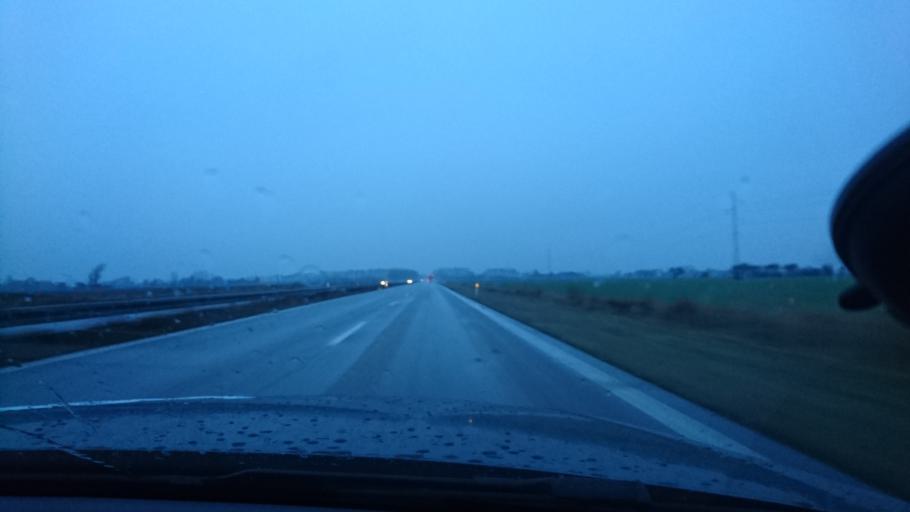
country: DK
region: Zealand
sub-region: Lolland Kommune
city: Rodby
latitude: 54.6865
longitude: 11.4034
